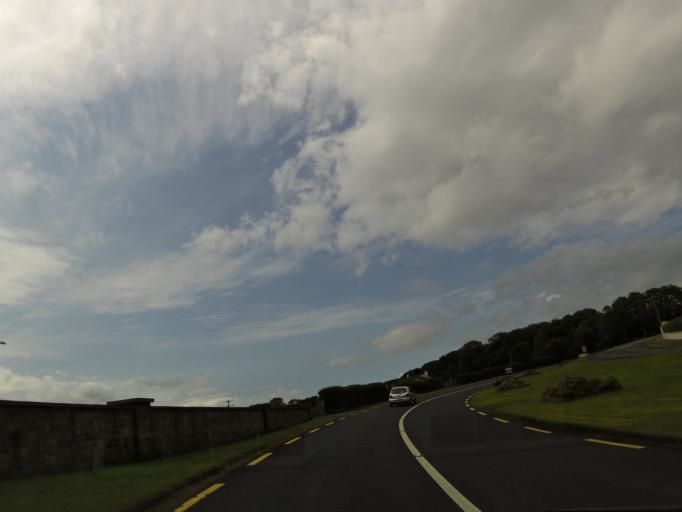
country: IE
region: Munster
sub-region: An Clar
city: Kilrush
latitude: 52.6423
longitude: -9.4913
